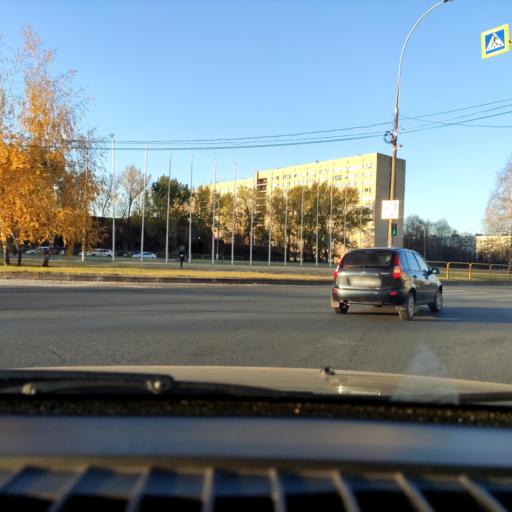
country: RU
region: Samara
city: Tol'yatti
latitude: 53.5294
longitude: 49.2814
